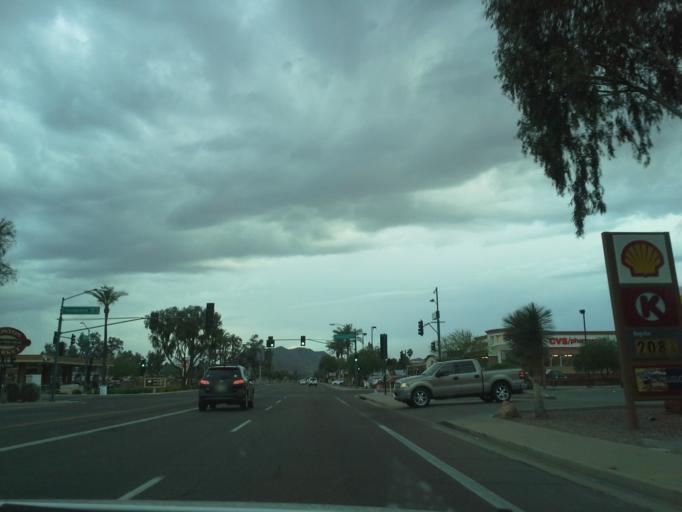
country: US
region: Arizona
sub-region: Maricopa County
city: Paradise Valley
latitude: 33.6126
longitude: -111.9960
